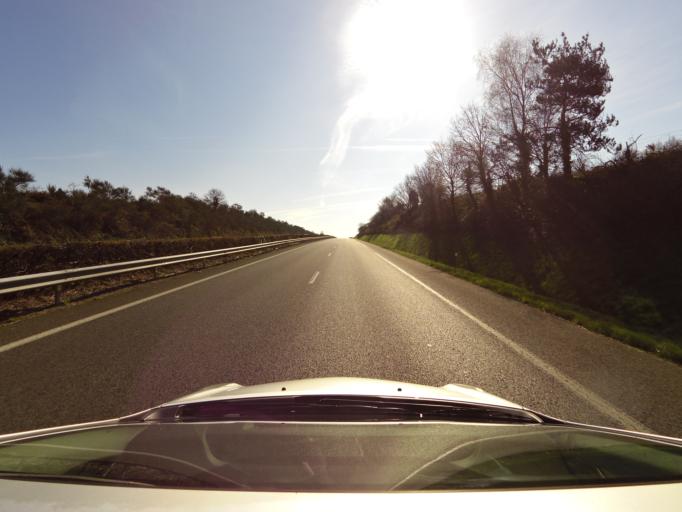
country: FR
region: Brittany
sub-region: Departement du Morbihan
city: Taupont
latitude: 47.9380
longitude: -2.4569
